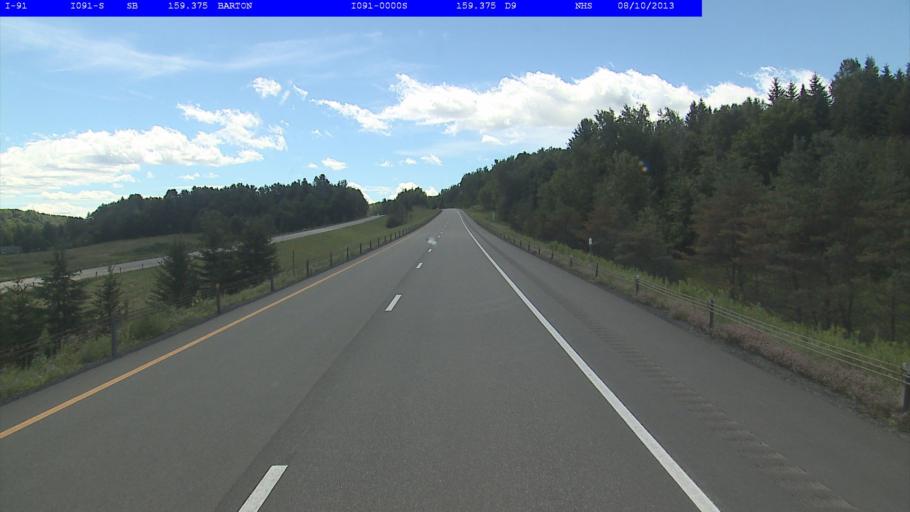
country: US
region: Vermont
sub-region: Orleans County
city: Newport
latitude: 44.7775
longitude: -72.2154
